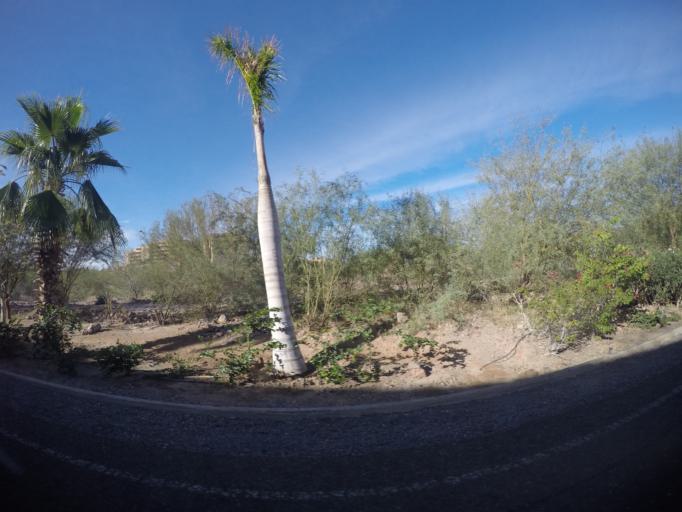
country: MX
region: Baja California Sur
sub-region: La Paz
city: La Paz
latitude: 24.1893
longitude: -110.2945
